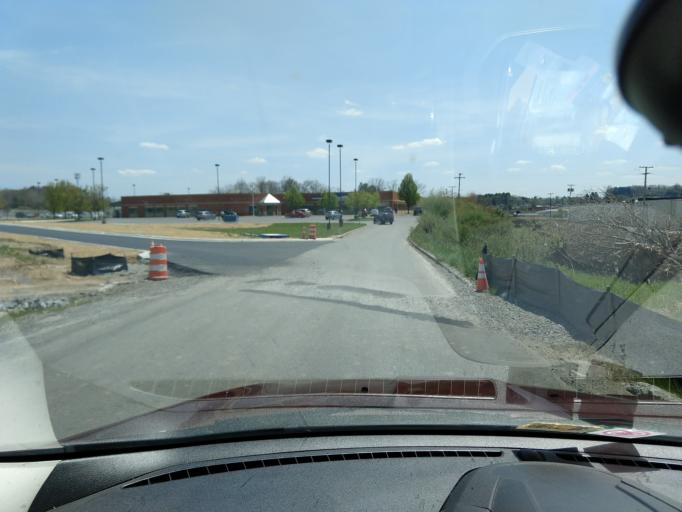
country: US
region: West Virginia
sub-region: Raleigh County
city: Stanaford
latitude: 37.8105
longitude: -81.1825
